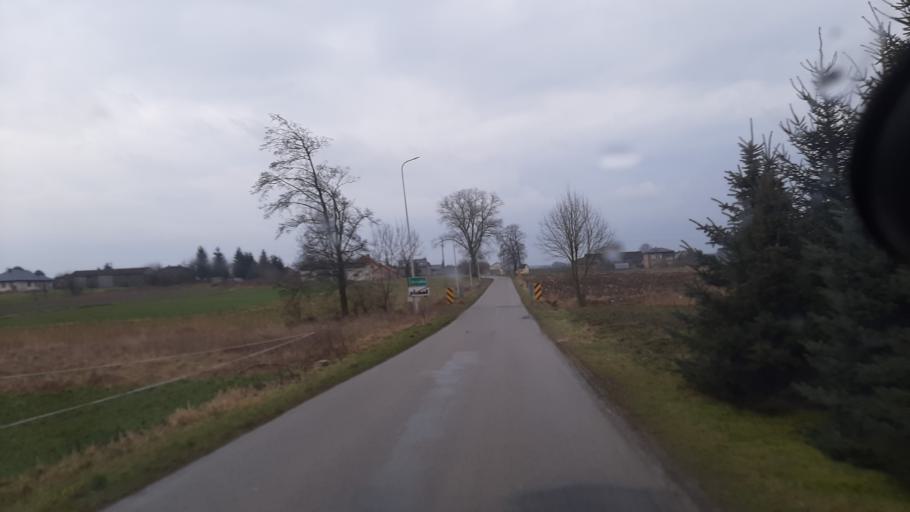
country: PL
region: Lublin Voivodeship
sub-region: Powiat lubelski
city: Jastkow
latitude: 51.3627
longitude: 22.4552
